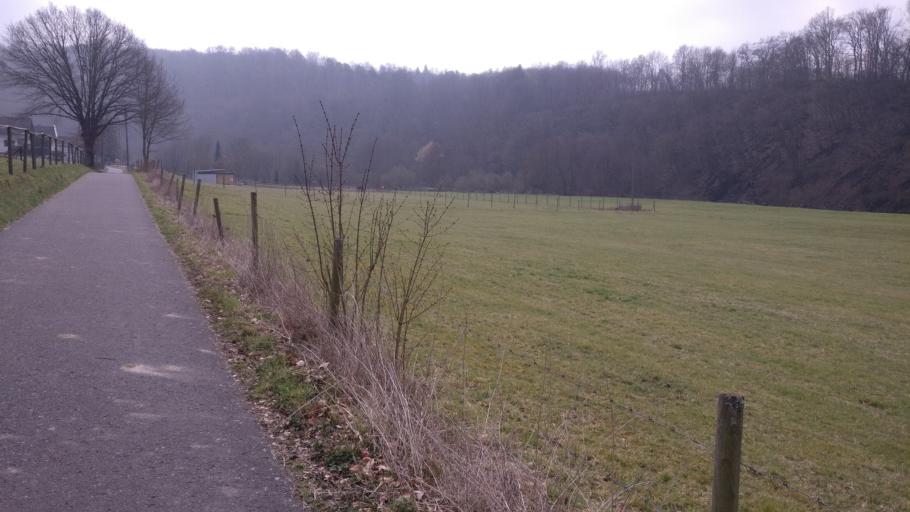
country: DE
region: Rheinland-Pfalz
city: Rossbach
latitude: 50.6210
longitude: 7.4214
